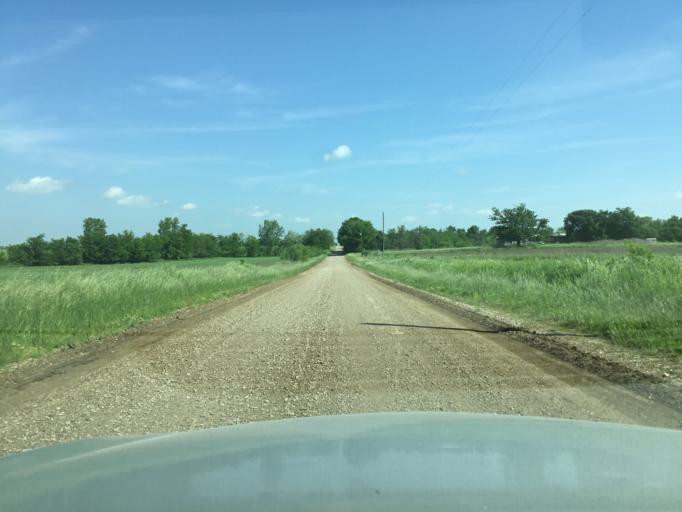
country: US
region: Kansas
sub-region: Labette County
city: Oswego
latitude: 37.1826
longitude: -95.1399
